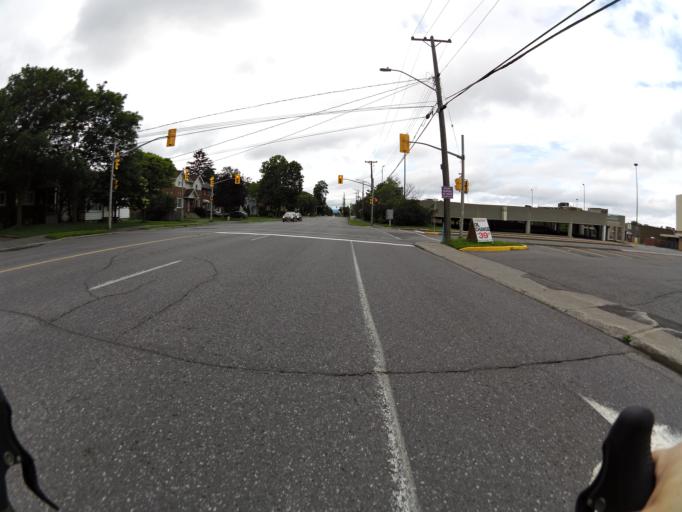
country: CA
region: Ontario
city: Bells Corners
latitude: 45.3716
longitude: -75.7714
